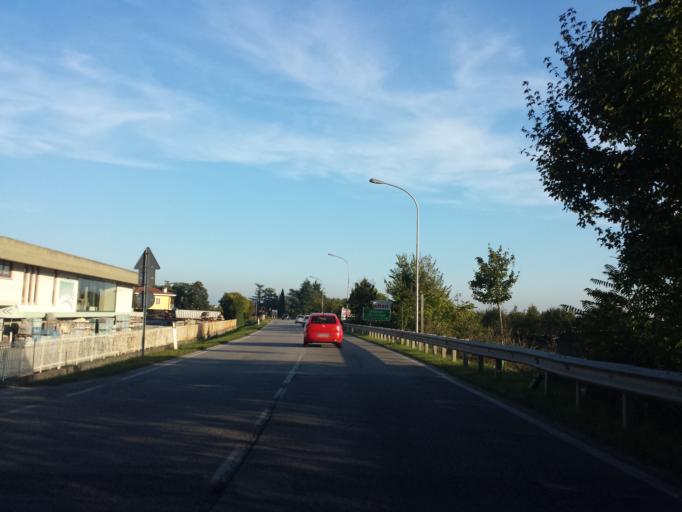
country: IT
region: Veneto
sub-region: Provincia di Vicenza
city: Isola Vicentina
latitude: 45.6244
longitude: 11.4507
